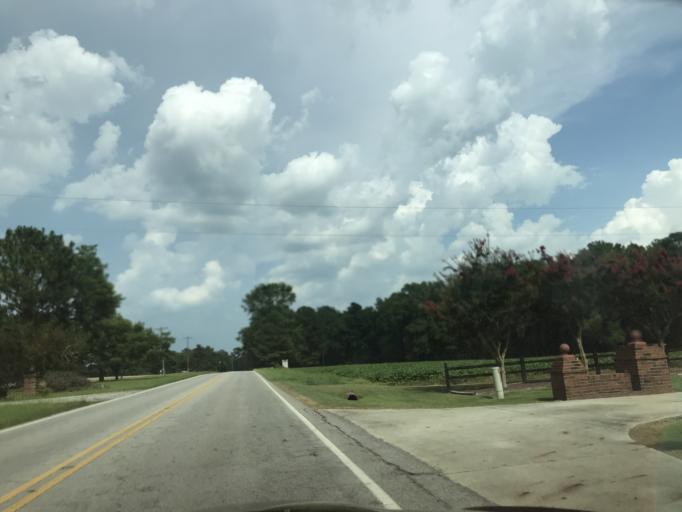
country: US
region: North Carolina
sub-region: Johnston County
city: Benson
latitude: 35.5142
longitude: -78.5410
